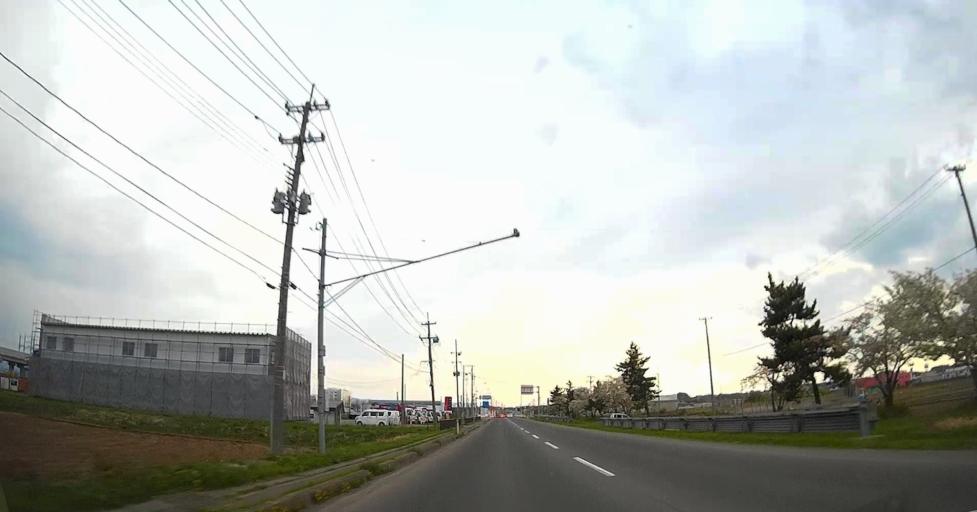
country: JP
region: Aomori
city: Aomori Shi
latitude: 40.8362
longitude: 140.6908
